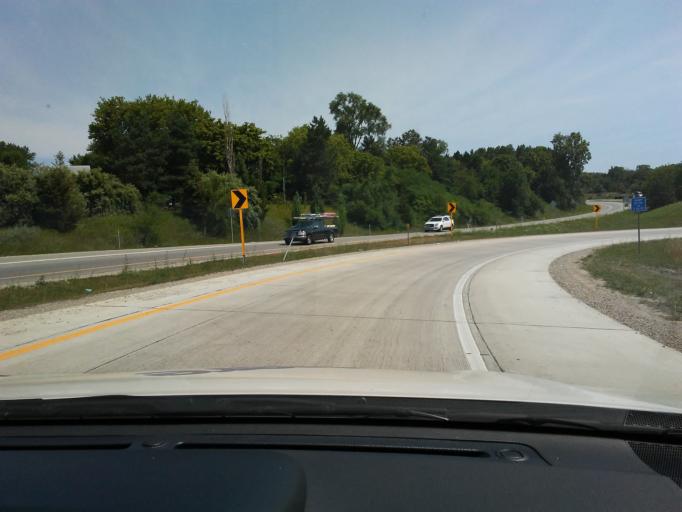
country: US
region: Michigan
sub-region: Livingston County
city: Brighton
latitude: 42.5269
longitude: -83.7576
